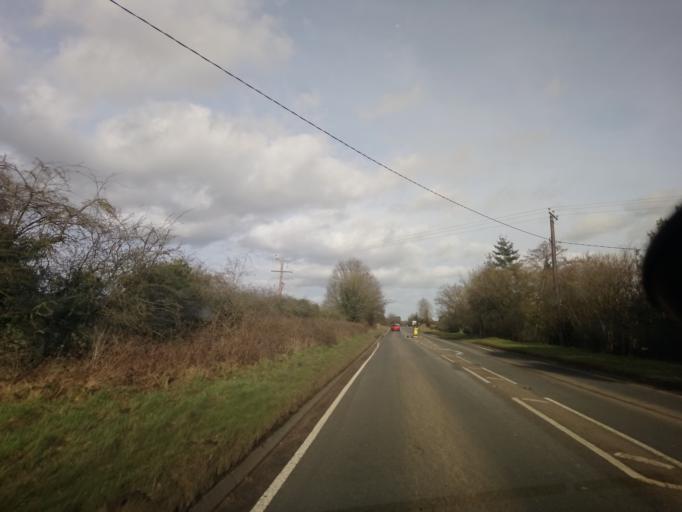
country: GB
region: England
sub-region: Shropshire
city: Stoke upon Tern
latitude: 52.7898
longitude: -2.5485
